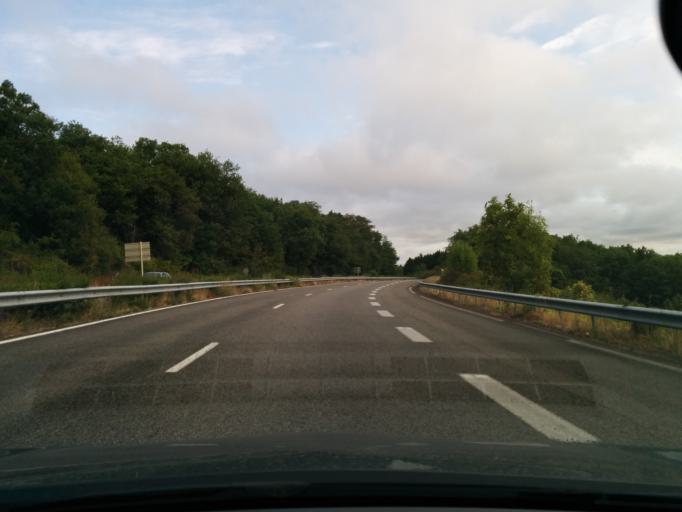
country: FR
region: Midi-Pyrenees
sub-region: Departement du Lot
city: Pradines
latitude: 44.5055
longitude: 1.4456
